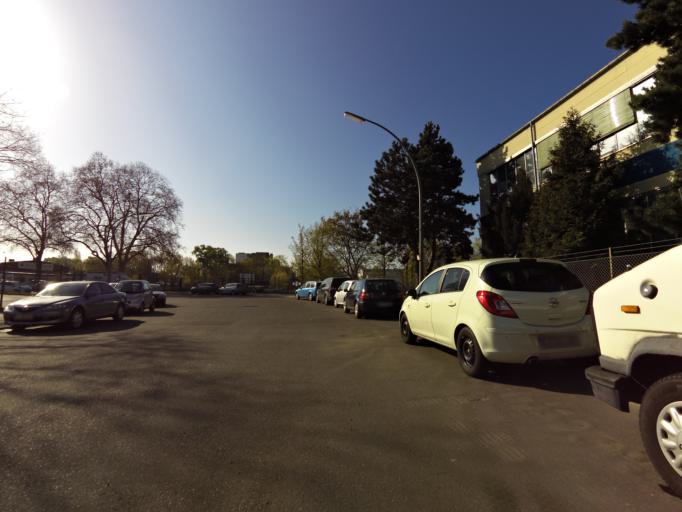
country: DE
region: Berlin
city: Britz
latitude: 52.4604
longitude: 13.4503
